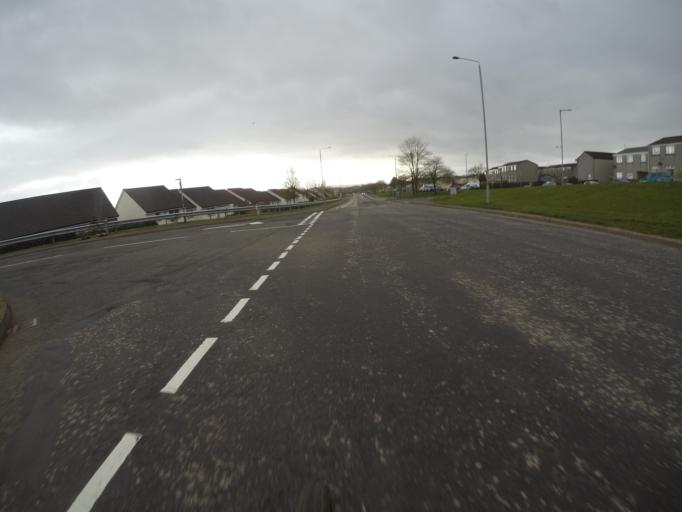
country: GB
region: Scotland
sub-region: East Ayrshire
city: Kilmarnock
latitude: 55.6226
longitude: -4.4686
